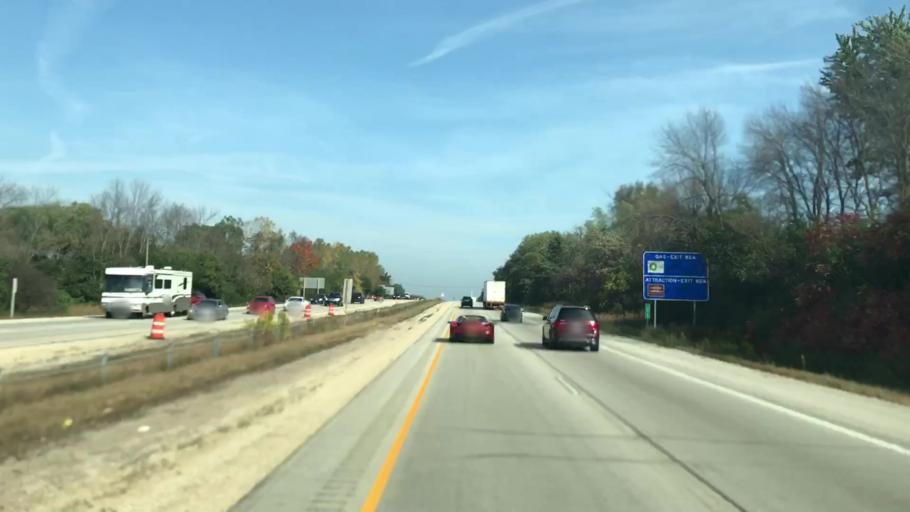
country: US
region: Wisconsin
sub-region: Milwaukee County
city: Fox Point
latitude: 43.1583
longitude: -87.9159
